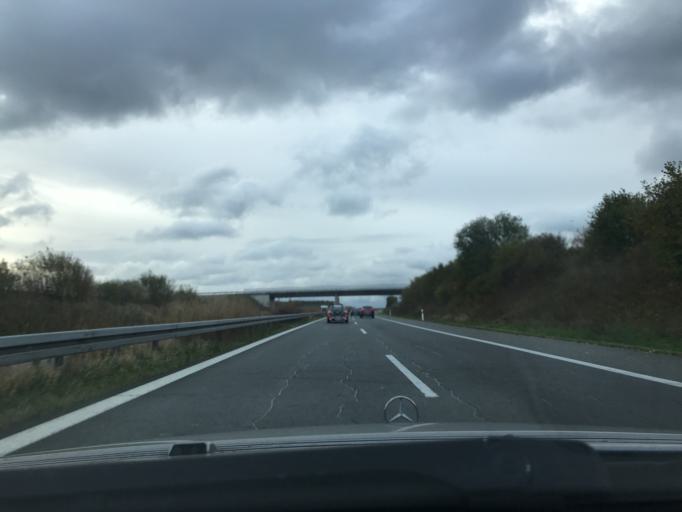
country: DE
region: Mecklenburg-Vorpommern
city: Brunn
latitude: 53.6399
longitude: 13.3698
